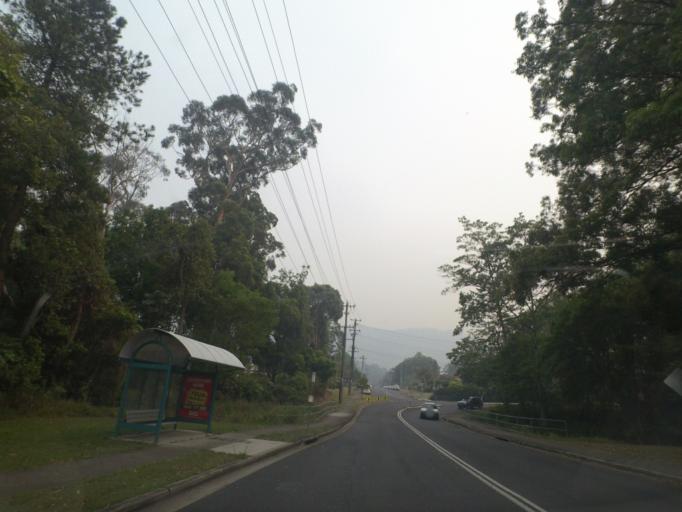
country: AU
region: New South Wales
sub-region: Coffs Harbour
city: Coffs Harbour
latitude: -30.2801
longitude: 153.1037
